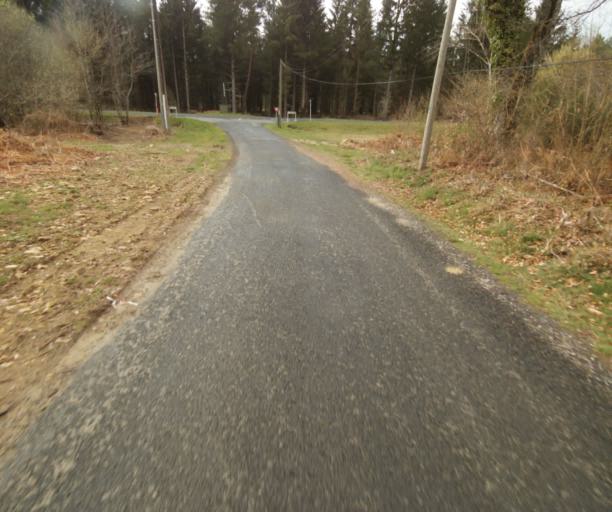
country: FR
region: Limousin
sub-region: Departement de la Correze
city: Saint-Privat
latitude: 45.2255
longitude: 2.0082
